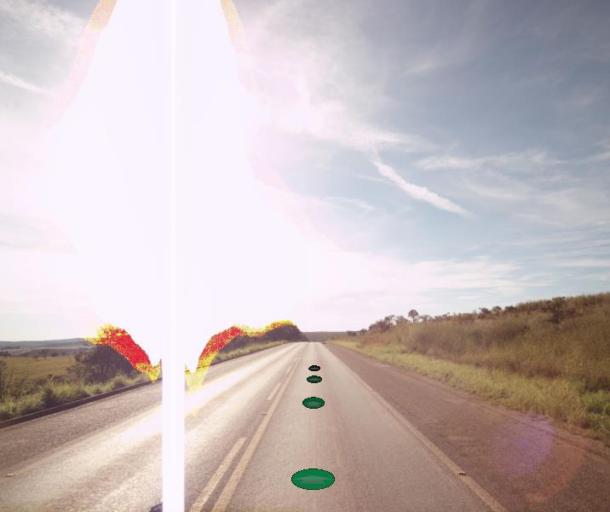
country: BR
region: Federal District
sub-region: Brasilia
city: Brasilia
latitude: -15.7435
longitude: -48.3654
